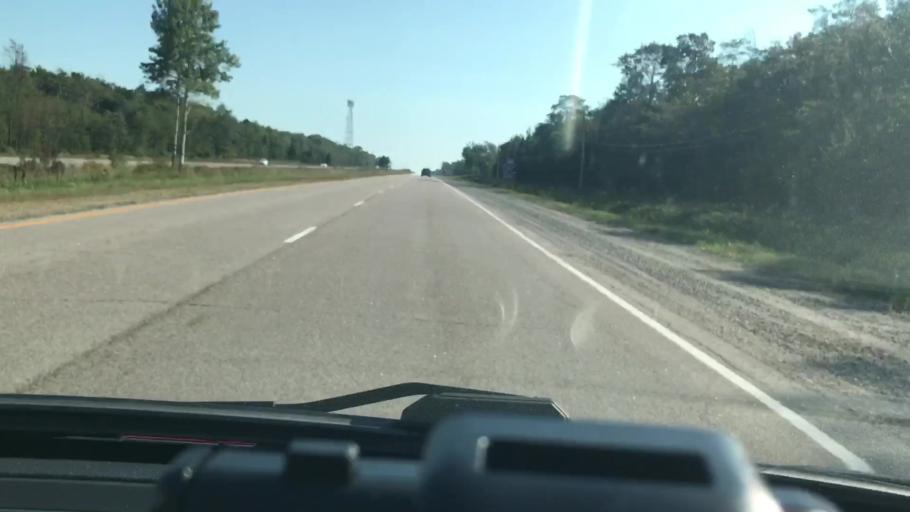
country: CA
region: Ontario
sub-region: Algoma
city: Sault Ste. Marie
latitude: 46.3967
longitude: -84.0679
